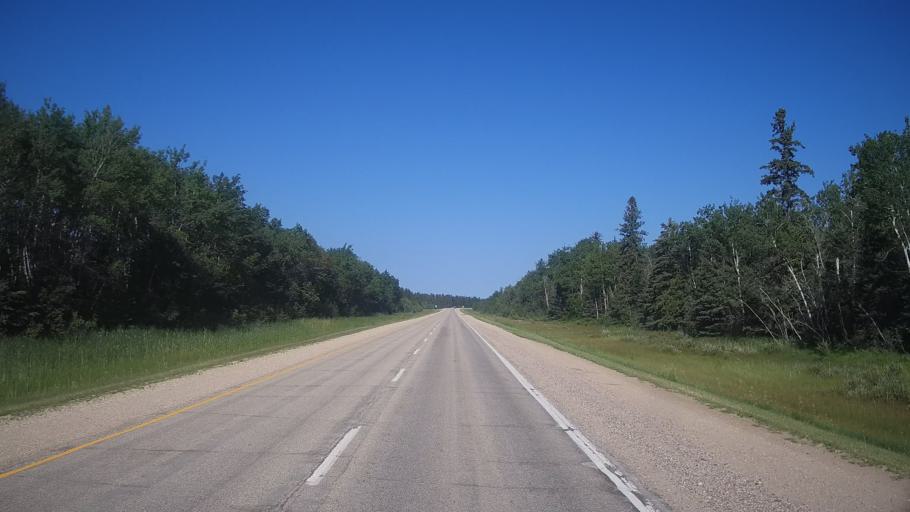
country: CA
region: Manitoba
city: La Broquerie
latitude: 49.6495
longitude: -95.9609
